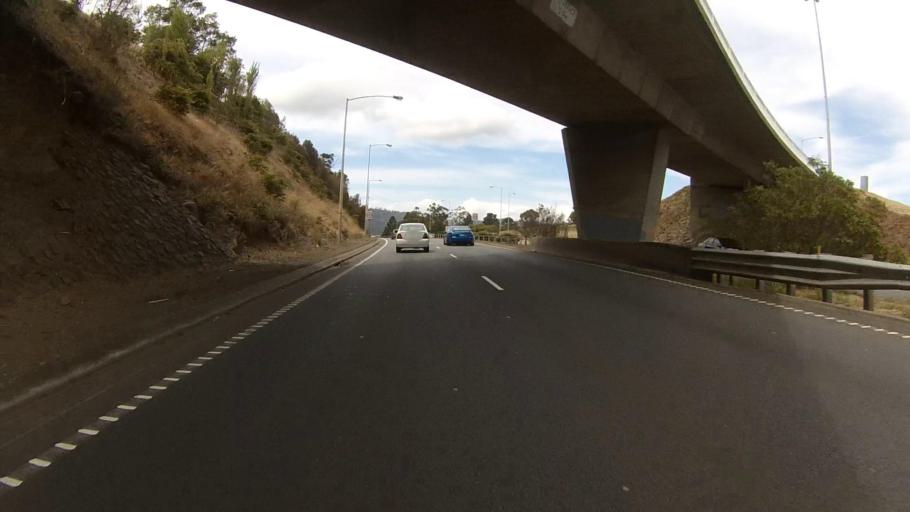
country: AU
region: Tasmania
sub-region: Clarence
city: Lindisfarne
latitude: -42.8623
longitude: 147.3629
